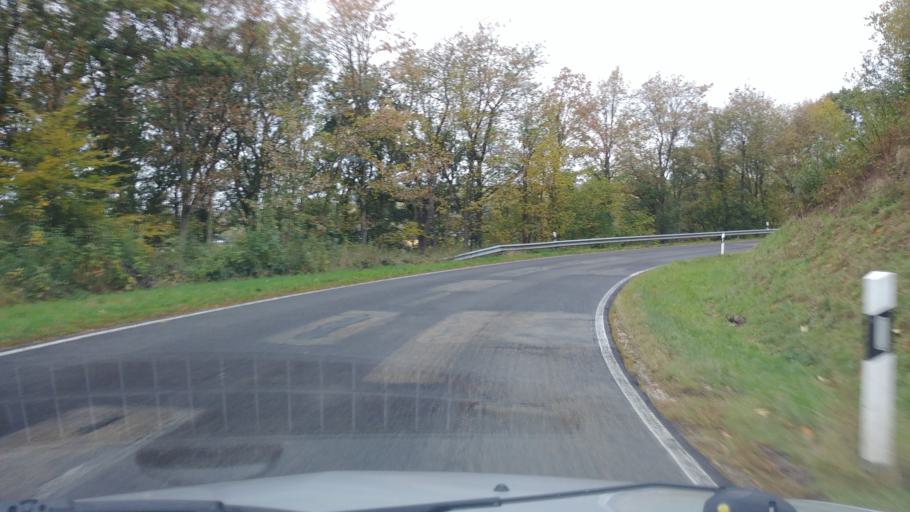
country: DE
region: Rheinland-Pfalz
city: Gornhausen
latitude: 49.8194
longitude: 7.0656
